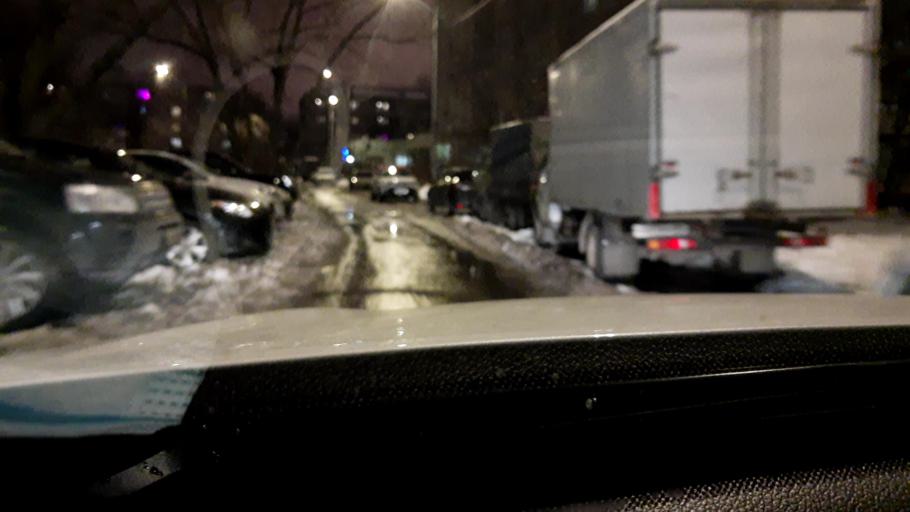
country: RU
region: Moskovskaya
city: Shcherbinka
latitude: 55.5064
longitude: 37.5701
